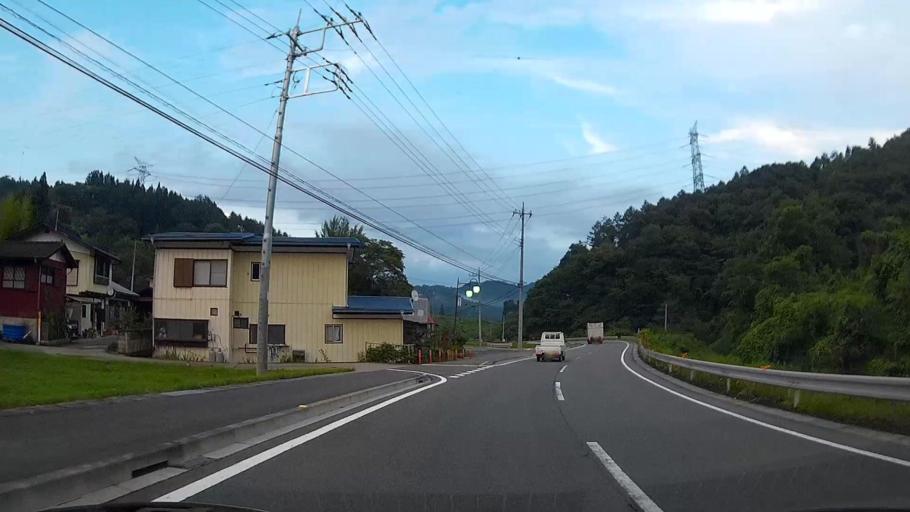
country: JP
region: Gunma
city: Nakanojomachi
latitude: 36.5272
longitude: 138.7384
